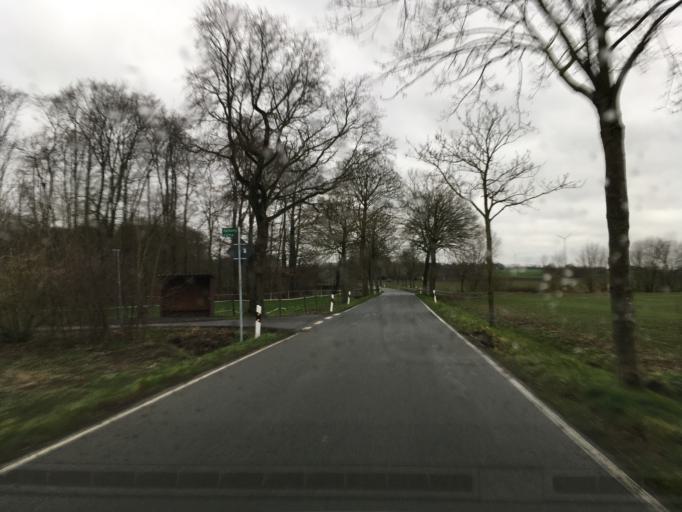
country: DE
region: North Rhine-Westphalia
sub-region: Regierungsbezirk Munster
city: Schoppingen
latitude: 52.0863
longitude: 7.1702
